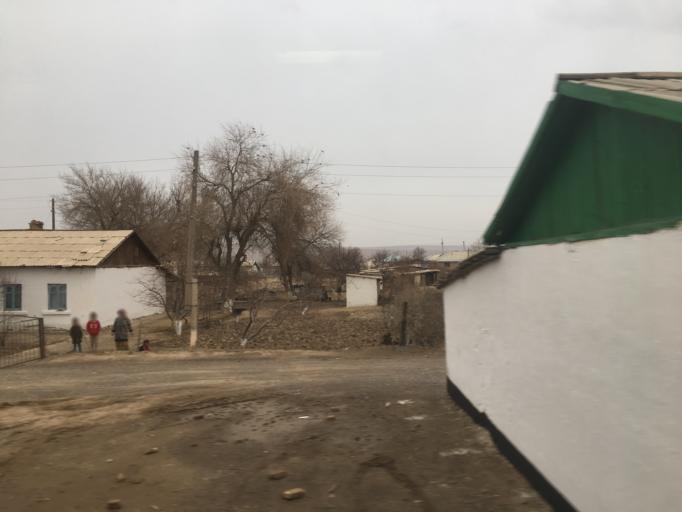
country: TM
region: Mary
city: Yoloeten
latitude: 36.5363
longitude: 62.5540
